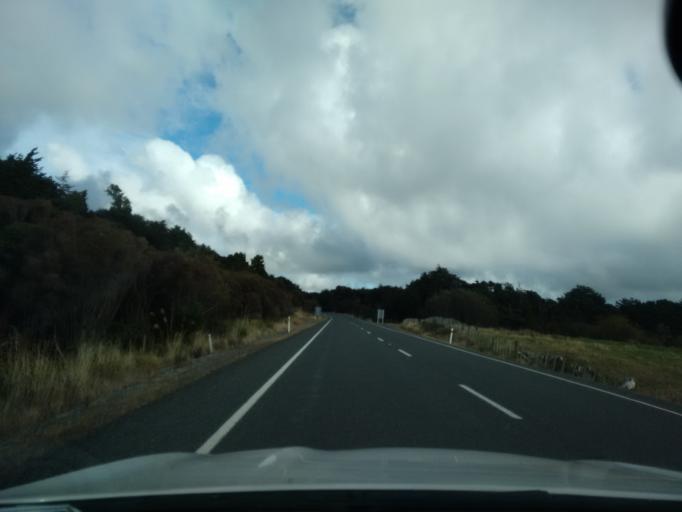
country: NZ
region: Manawatu-Wanganui
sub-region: Ruapehu District
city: Waiouru
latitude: -39.2980
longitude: 175.3881
